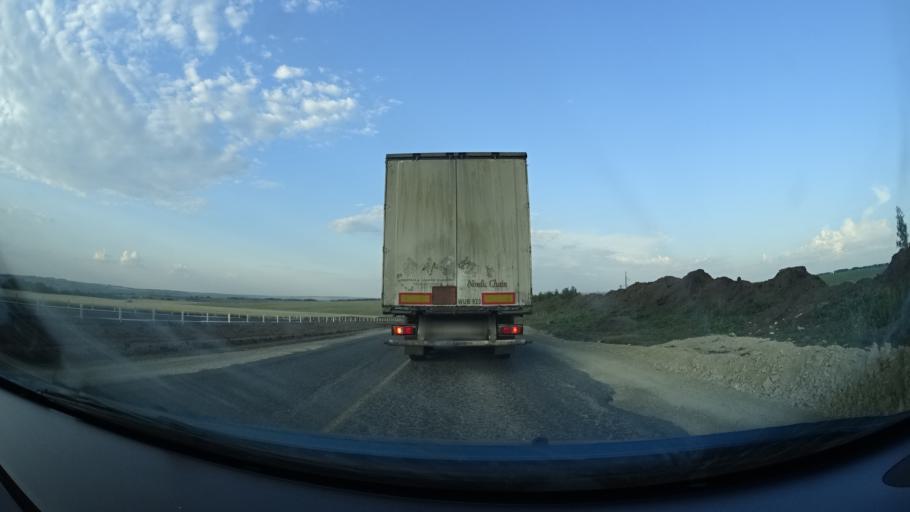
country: RU
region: Samara
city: Kamyshla
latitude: 54.0376
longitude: 51.9567
